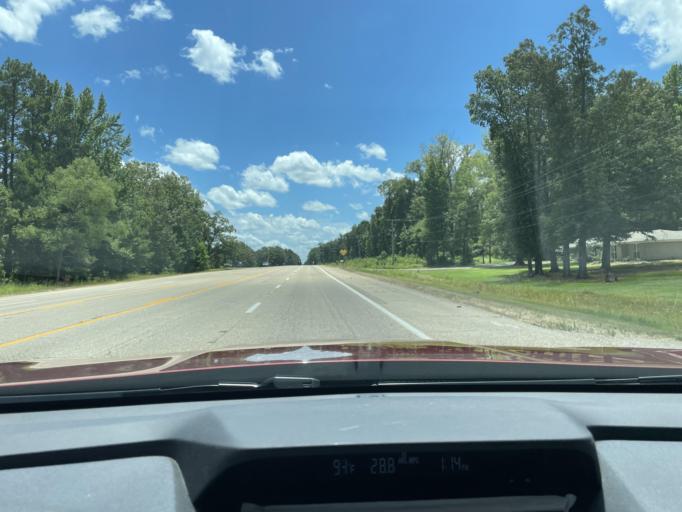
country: US
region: Arkansas
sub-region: Drew County
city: Monticello
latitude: 33.6623
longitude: -91.8034
